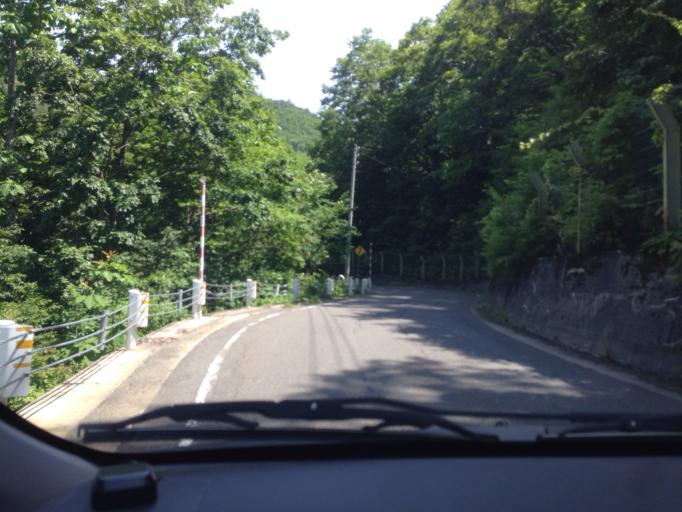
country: JP
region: Fukushima
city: Kitakata
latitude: 37.2816
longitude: 139.6854
